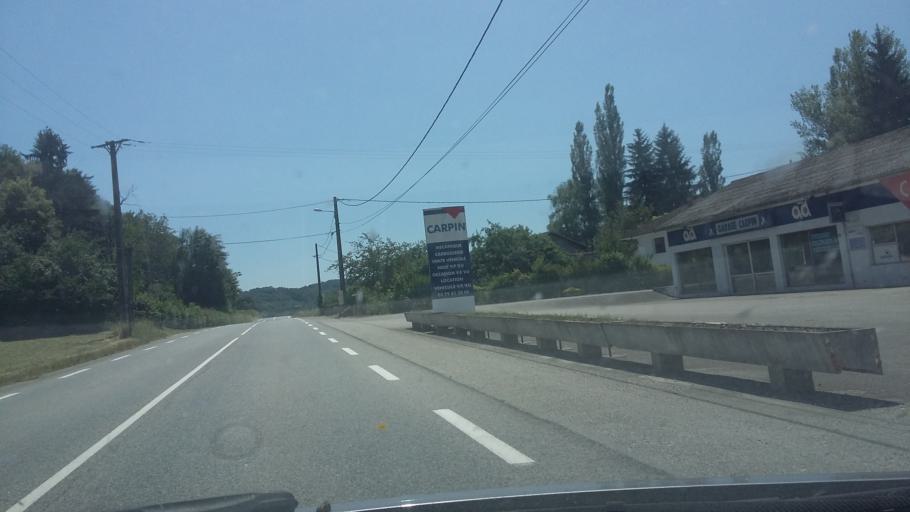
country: FR
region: Rhone-Alpes
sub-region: Departement de l'Ain
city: Belley
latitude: 45.7968
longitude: 5.6822
